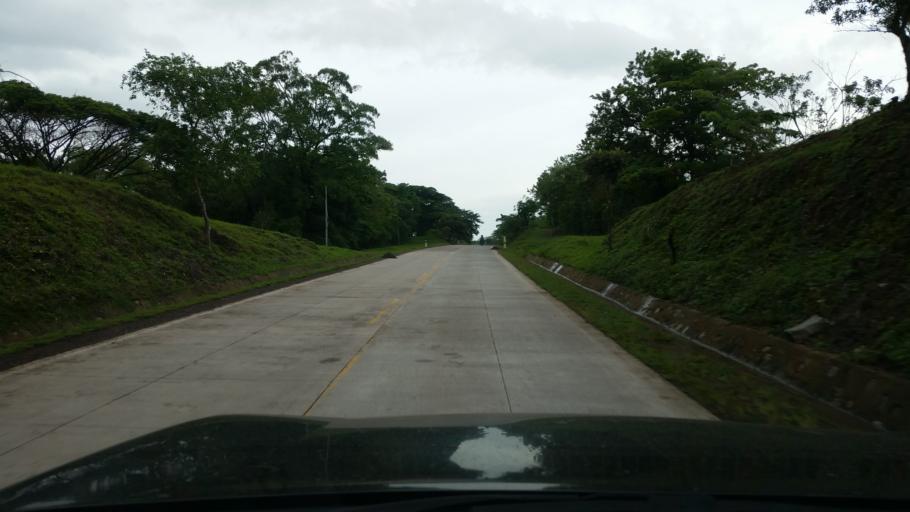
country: NI
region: Matagalpa
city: Rio Blanco
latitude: 13.1449
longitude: -84.9939
